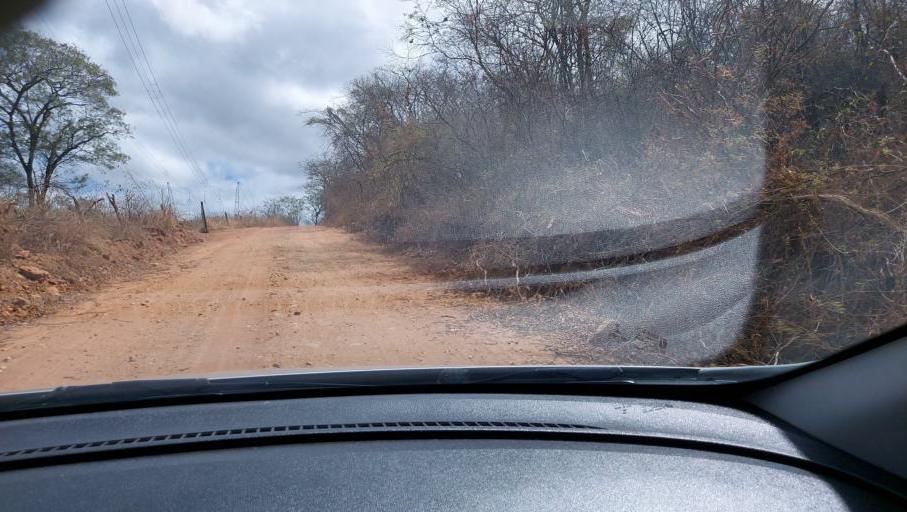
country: BR
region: Bahia
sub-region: Oliveira Dos Brejinhos
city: Beira Rio
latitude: -12.0881
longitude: -42.5434
